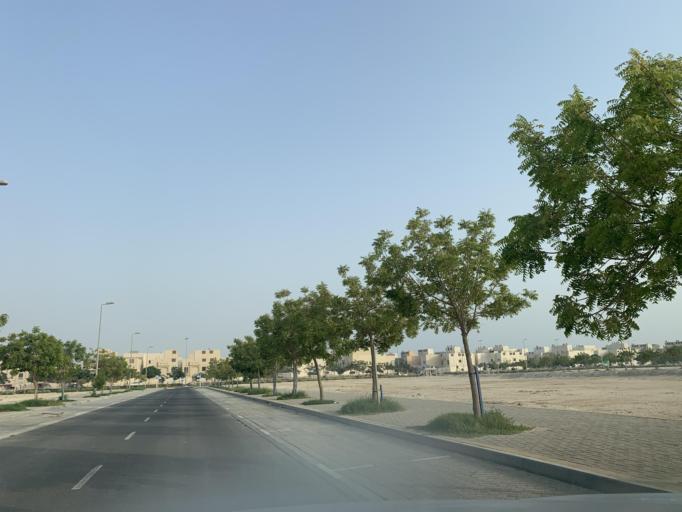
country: BH
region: Manama
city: Jidd Hafs
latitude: 26.2249
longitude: 50.4443
